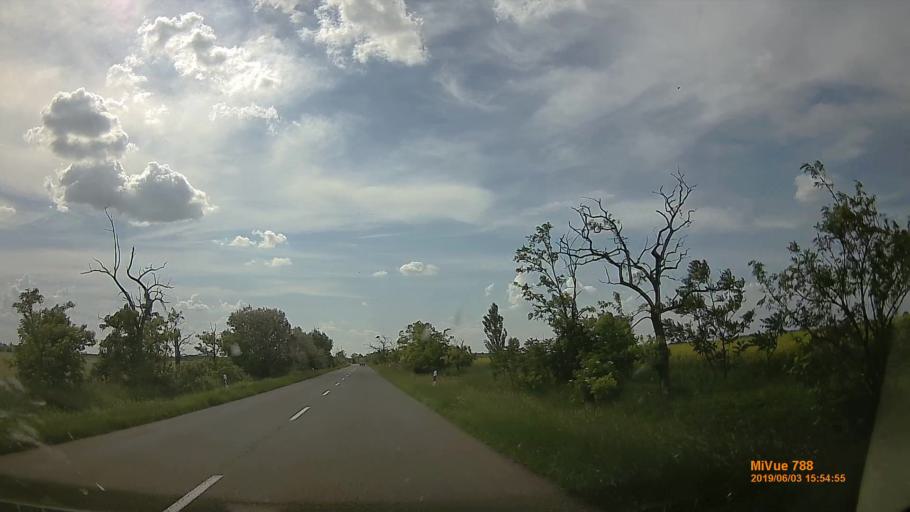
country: HU
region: Bacs-Kiskun
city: Akaszto
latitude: 46.7501
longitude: 19.1206
